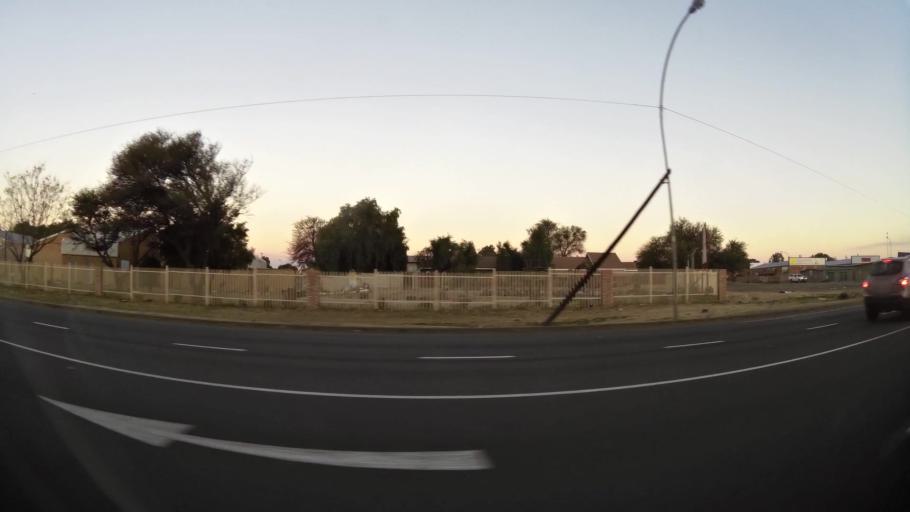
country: ZA
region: Northern Cape
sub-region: Frances Baard District Municipality
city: Kimberley
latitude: -28.7200
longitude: 24.7732
